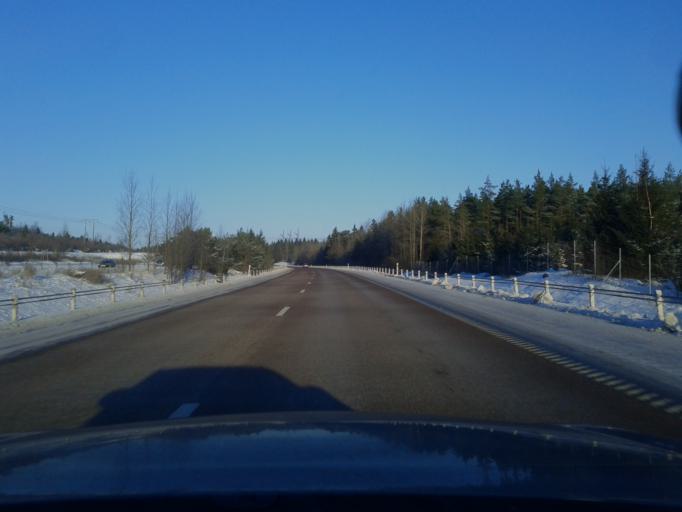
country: SE
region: Stockholm
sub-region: Sigtuna Kommun
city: Marsta
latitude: 59.6790
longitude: 17.8696
